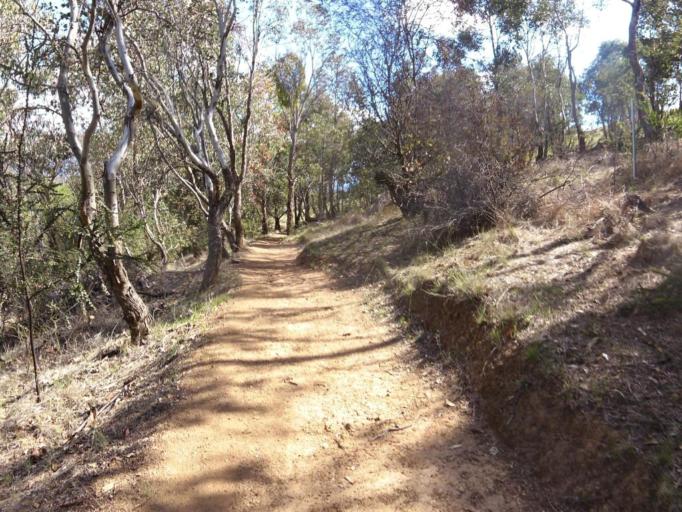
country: AU
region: Australian Capital Territory
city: Belconnen
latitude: -35.1516
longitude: 149.0870
